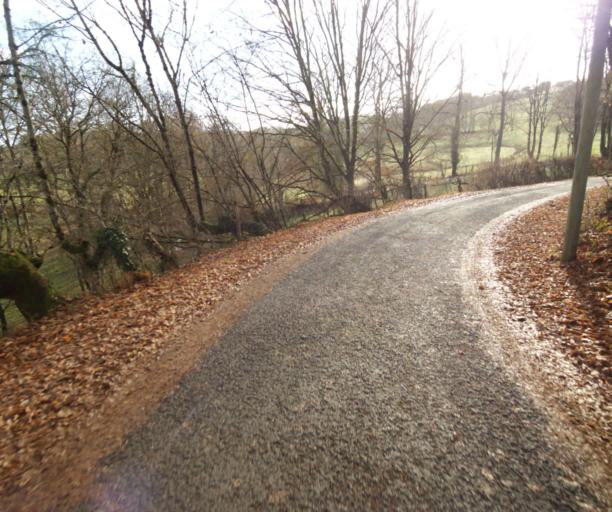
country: FR
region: Limousin
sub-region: Departement de la Correze
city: Sainte-Fereole
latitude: 45.2527
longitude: 1.6062
